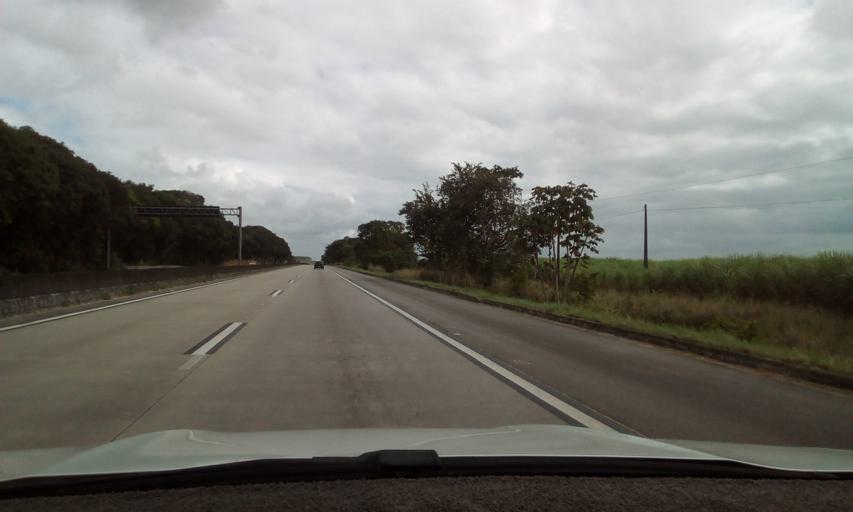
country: BR
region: Paraiba
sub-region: Santa Rita
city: Santa Rita
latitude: -7.0757
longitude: -34.9918
